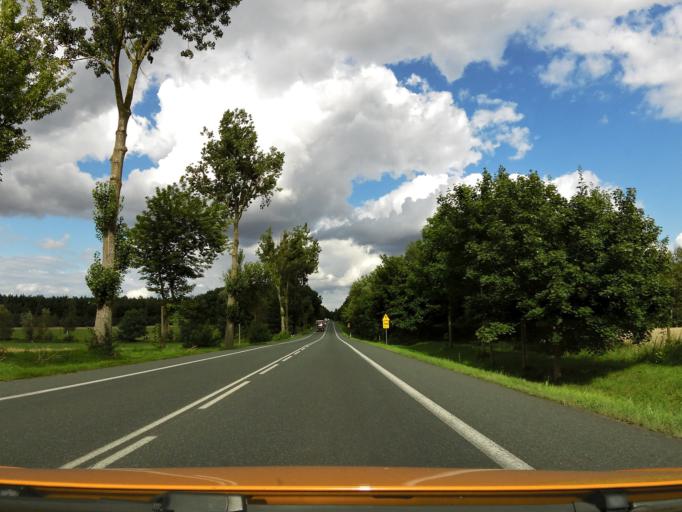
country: PL
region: West Pomeranian Voivodeship
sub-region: Powiat kolobrzeski
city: Ryman
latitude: 53.9113
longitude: 15.4454
